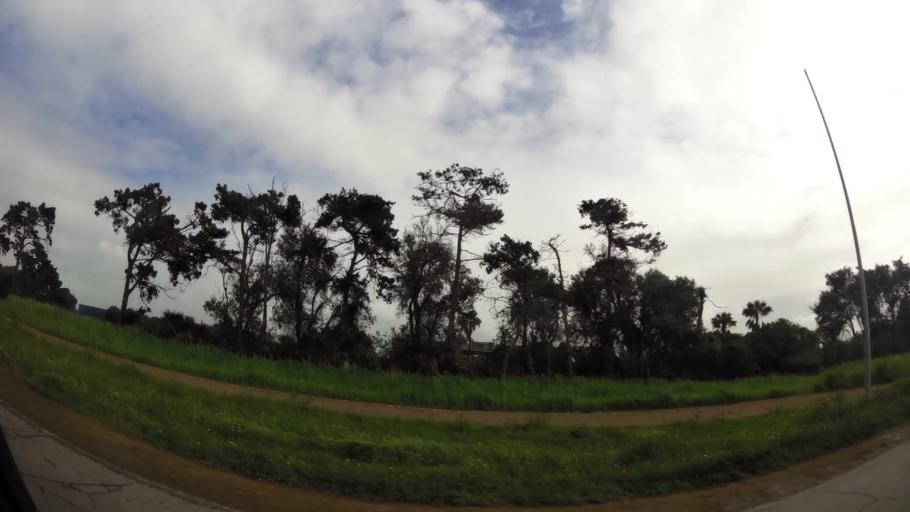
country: MA
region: Grand Casablanca
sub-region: Mohammedia
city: Mohammedia
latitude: 33.6400
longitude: -7.4388
